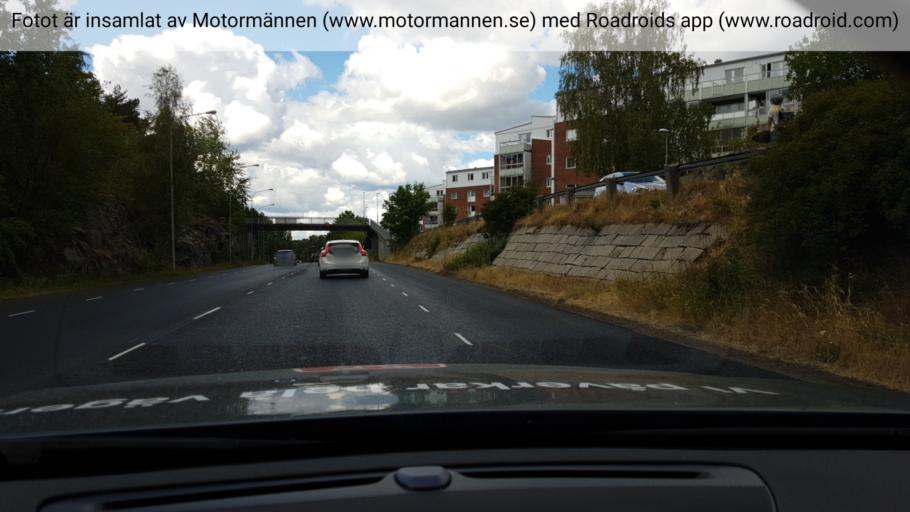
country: SE
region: Stockholm
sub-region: Vaxholms Kommun
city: Resaro
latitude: 59.4038
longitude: 18.3246
